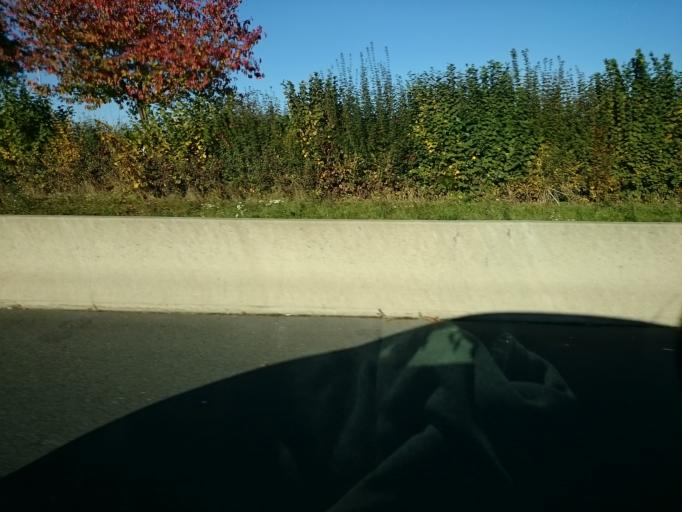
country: FR
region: Brittany
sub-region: Departement d'Ille-et-Vilaine
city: Pace
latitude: 48.1359
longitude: -1.7663
